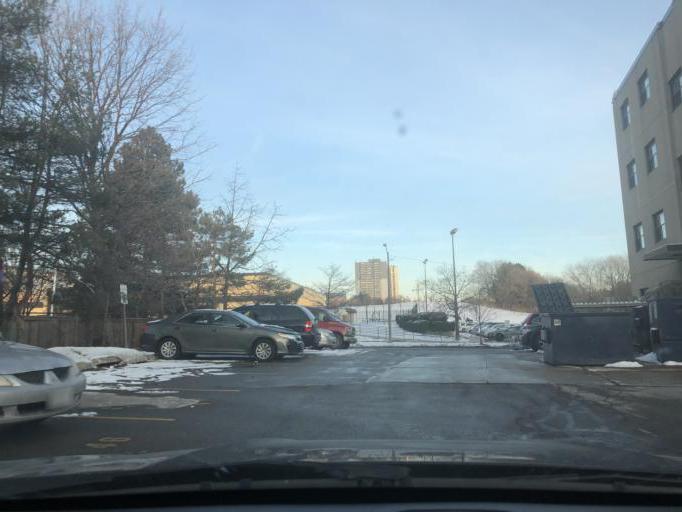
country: CA
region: Ontario
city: Toronto
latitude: 43.7054
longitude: -79.4879
